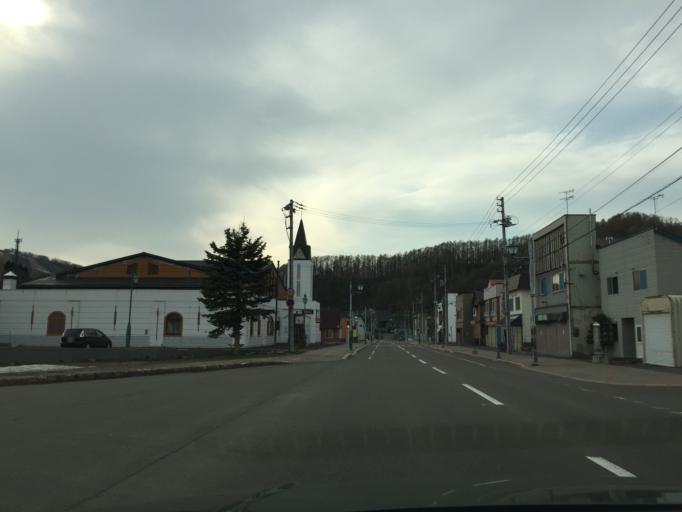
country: JP
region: Hokkaido
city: Utashinai
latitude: 43.5213
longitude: 142.0426
